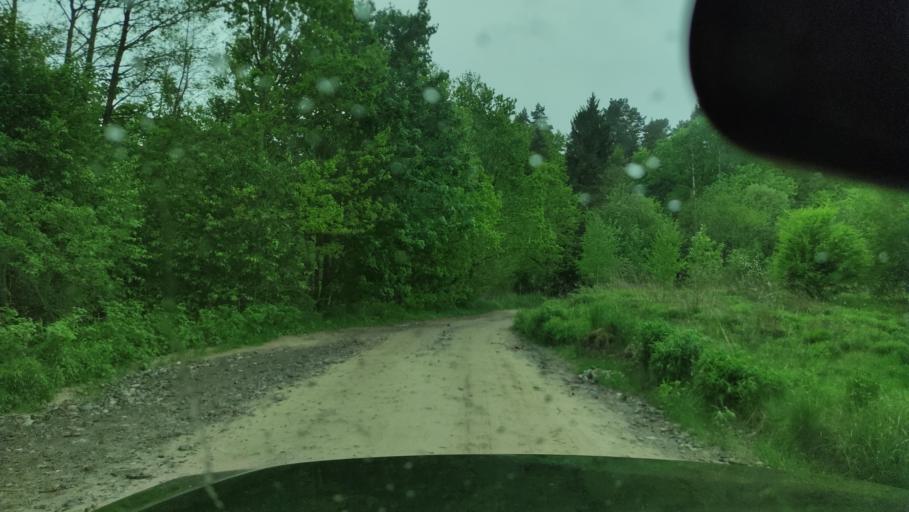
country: PL
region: Warmian-Masurian Voivodeship
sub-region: Powiat olsztynski
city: Olsztyn
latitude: 53.7612
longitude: 20.5231
